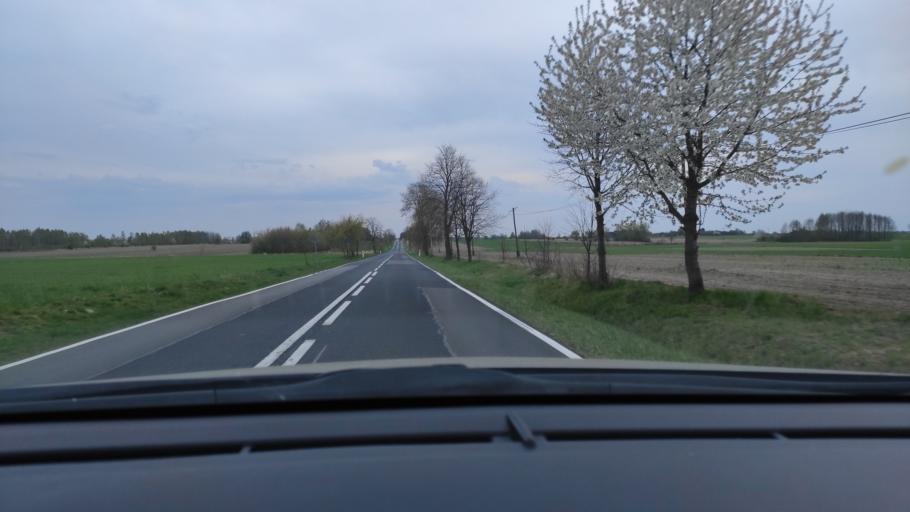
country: PL
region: Masovian Voivodeship
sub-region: Powiat zwolenski
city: Zwolen
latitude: 51.3777
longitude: 21.5627
